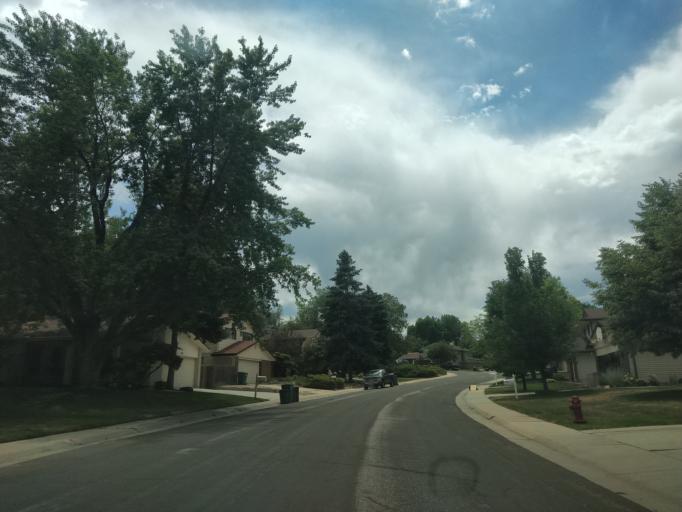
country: US
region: Colorado
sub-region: Jefferson County
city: Lakewood
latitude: 39.6864
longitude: -105.1223
